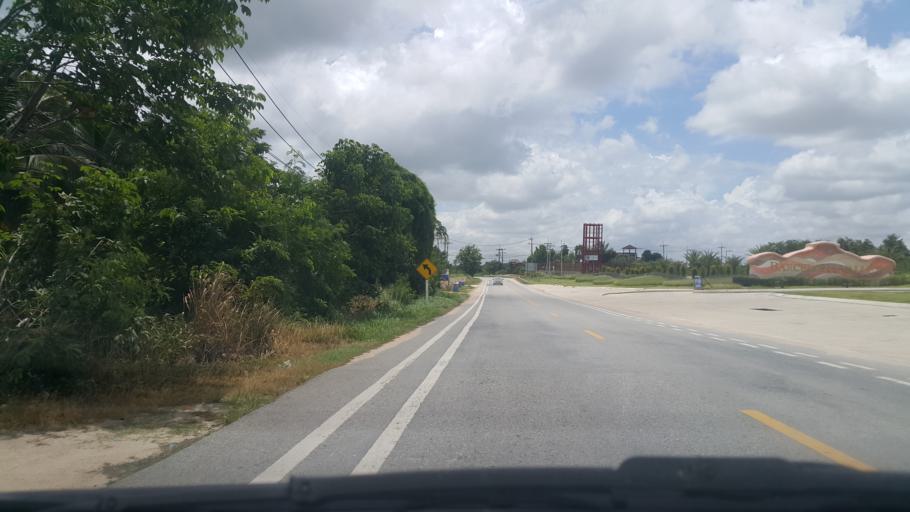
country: TH
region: Rayong
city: Ban Chang
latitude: 12.8123
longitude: 101.0593
